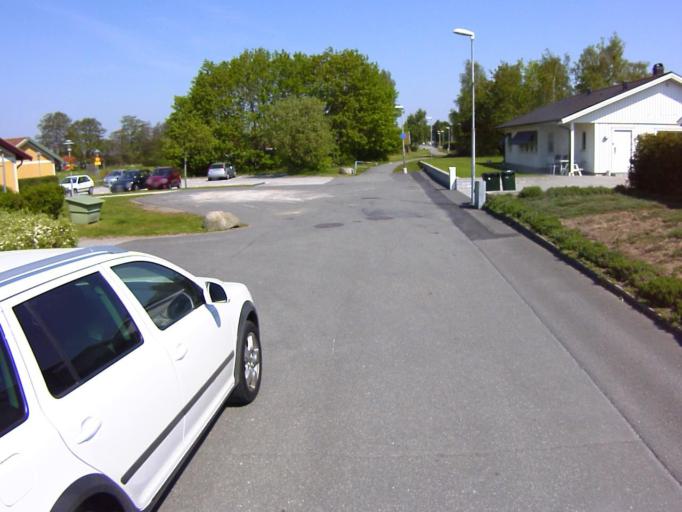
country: SE
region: Skane
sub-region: Kristianstads Kommun
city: Ahus
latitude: 55.9789
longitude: 14.2688
